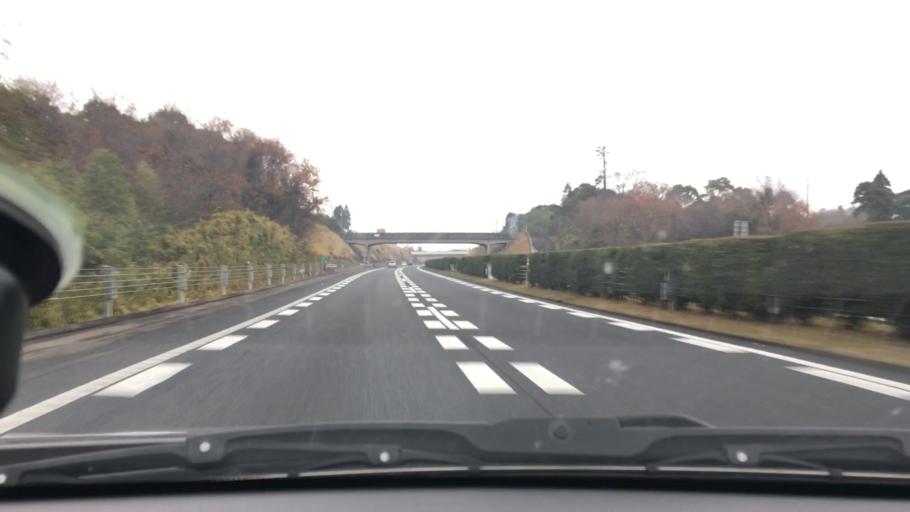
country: JP
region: Chiba
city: Narita
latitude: 35.7980
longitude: 140.3566
